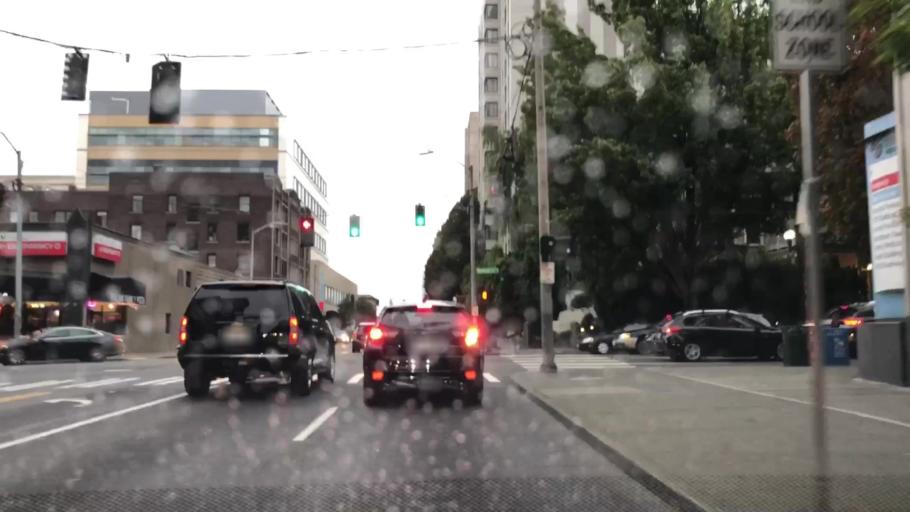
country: US
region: Washington
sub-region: Kitsap County
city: Manchester
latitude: 47.5770
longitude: -122.4949
